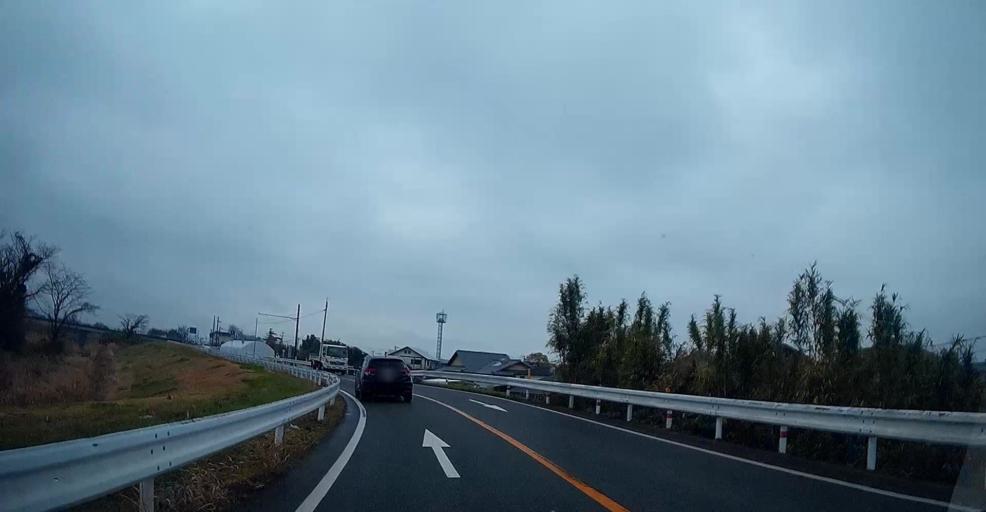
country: JP
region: Kumamoto
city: Kumamoto
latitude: 32.7547
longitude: 130.7403
